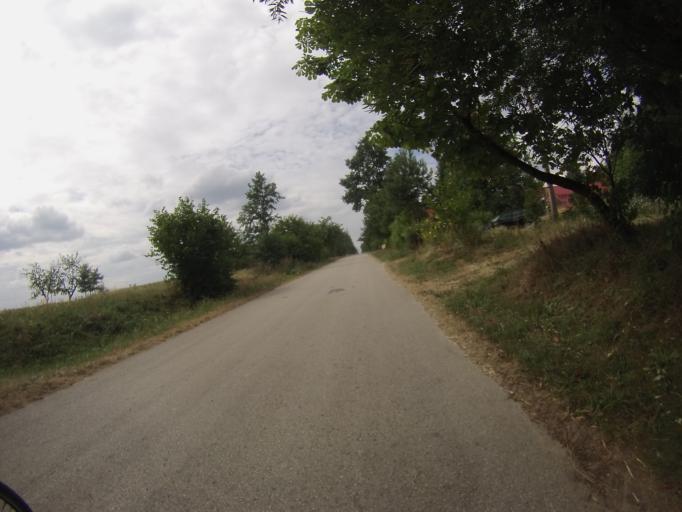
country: PL
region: Swietokrzyskie
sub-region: Powiat kielecki
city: Lagow
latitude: 50.7430
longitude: 21.1033
